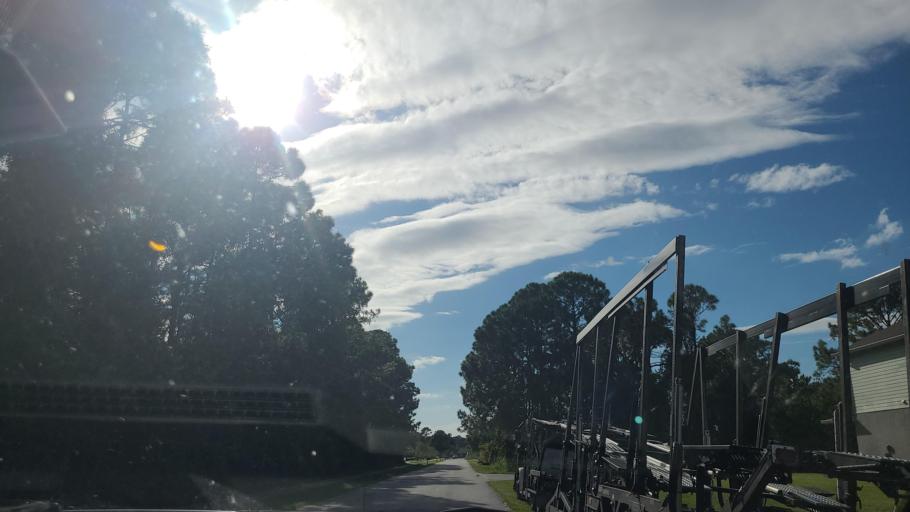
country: US
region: Florida
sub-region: Brevard County
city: Palm Bay
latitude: 27.9807
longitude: -80.6433
